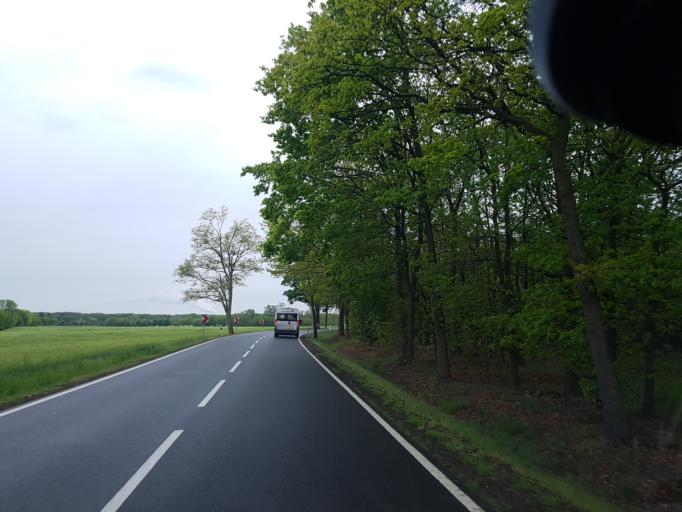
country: DE
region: Saxony
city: Gross Duben
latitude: 51.6204
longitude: 14.4981
